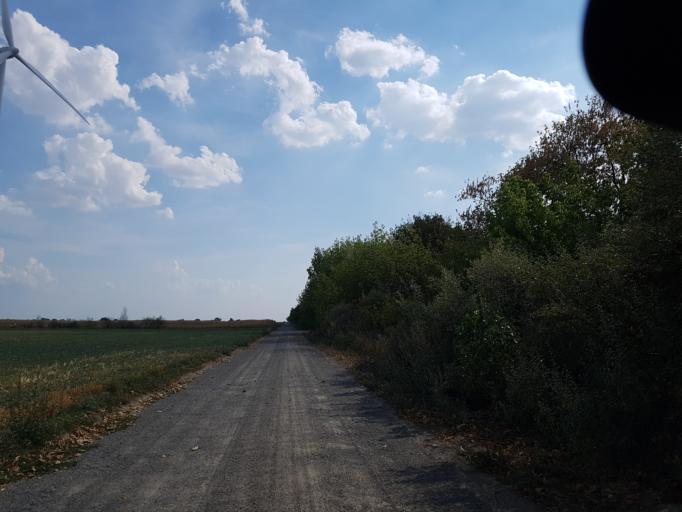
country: DE
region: Brandenburg
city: Treuenbrietzen
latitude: 52.0067
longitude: 12.8688
